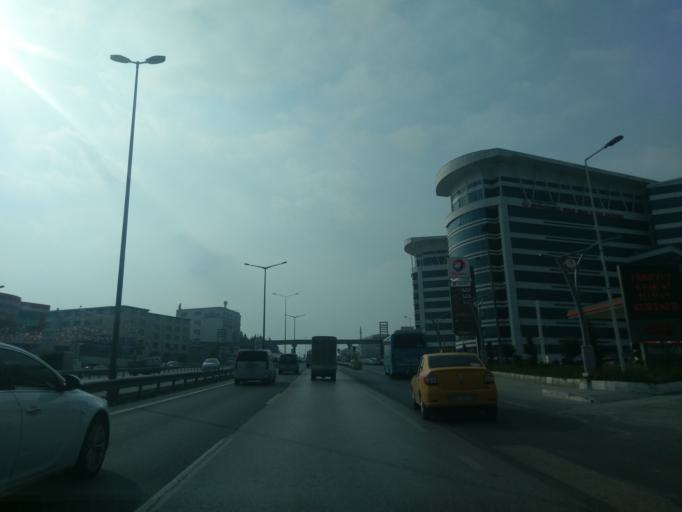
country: TR
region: Istanbul
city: Mimarsinan
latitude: 41.0169
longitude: 28.5581
